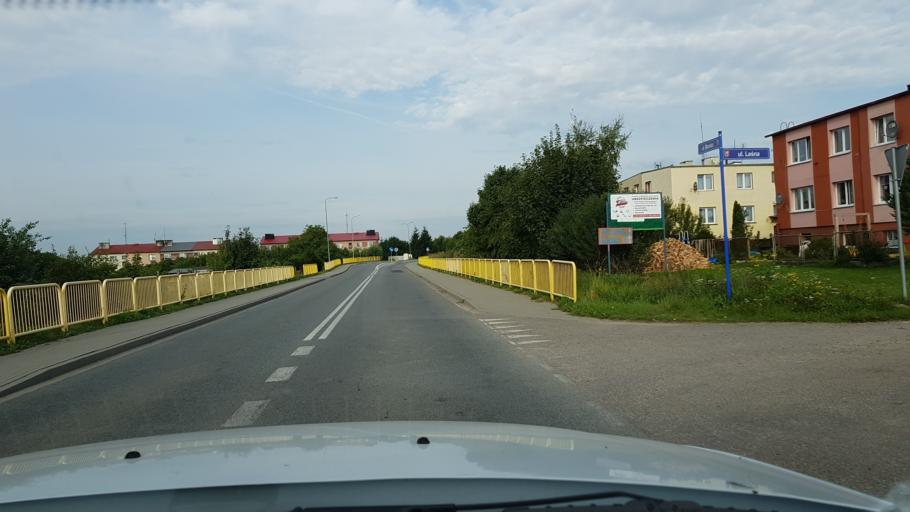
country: PL
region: West Pomeranian Voivodeship
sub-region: Powiat slawienski
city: Slawno
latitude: 54.3705
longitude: 16.6569
